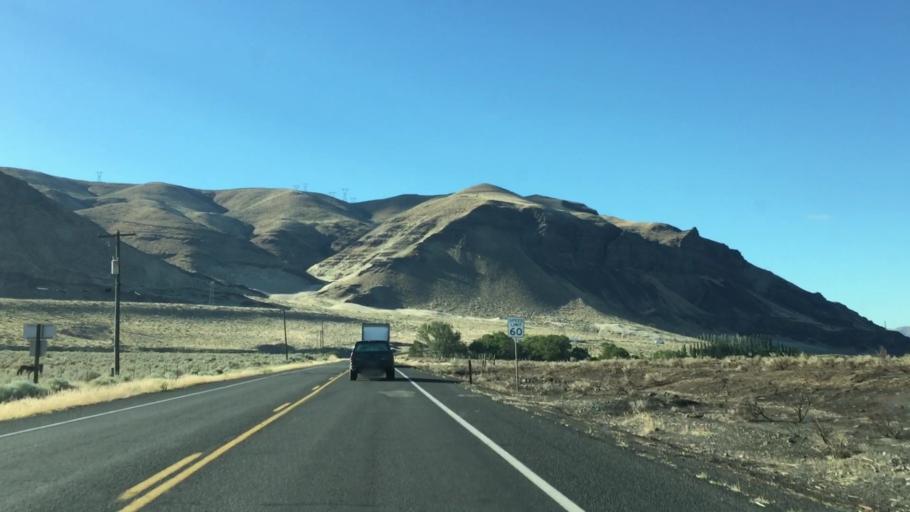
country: US
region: Washington
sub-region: Grant County
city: Mattawa
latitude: 46.8200
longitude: -119.9245
